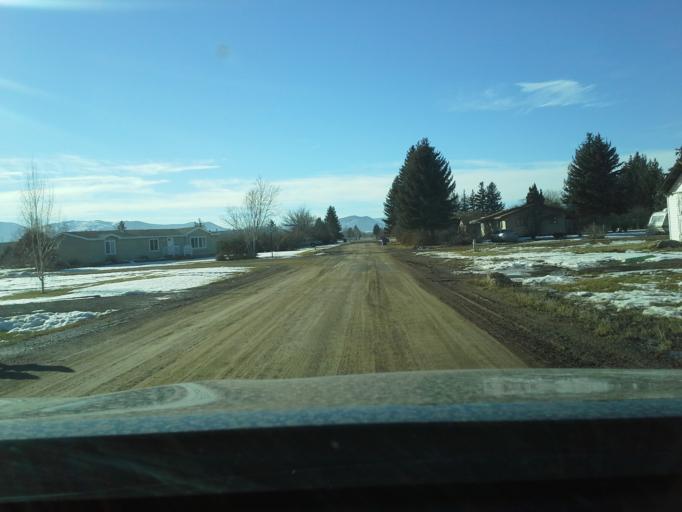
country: US
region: Montana
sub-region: Lewis and Clark County
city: East Helena
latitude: 46.5915
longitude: -111.9009
